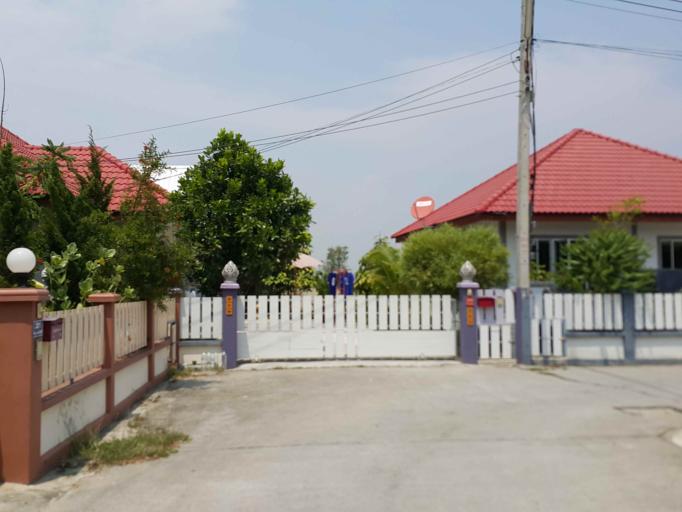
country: TH
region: Chiang Mai
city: San Kamphaeng
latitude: 18.7919
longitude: 99.0905
